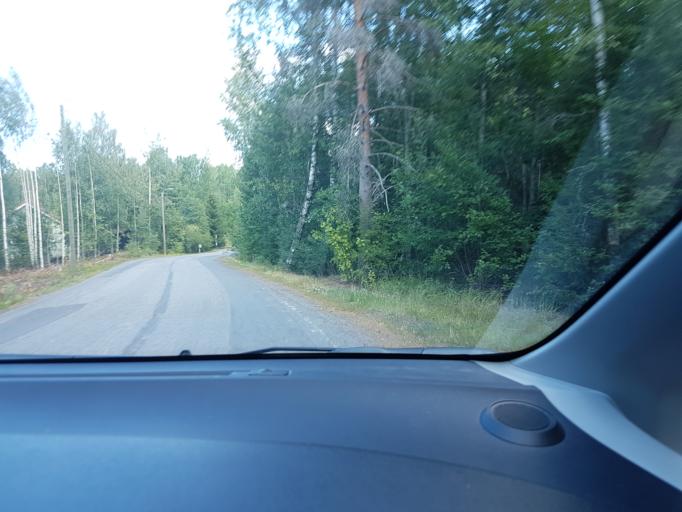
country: FI
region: Uusimaa
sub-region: Helsinki
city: Kilo
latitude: 60.3277
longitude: 24.7685
